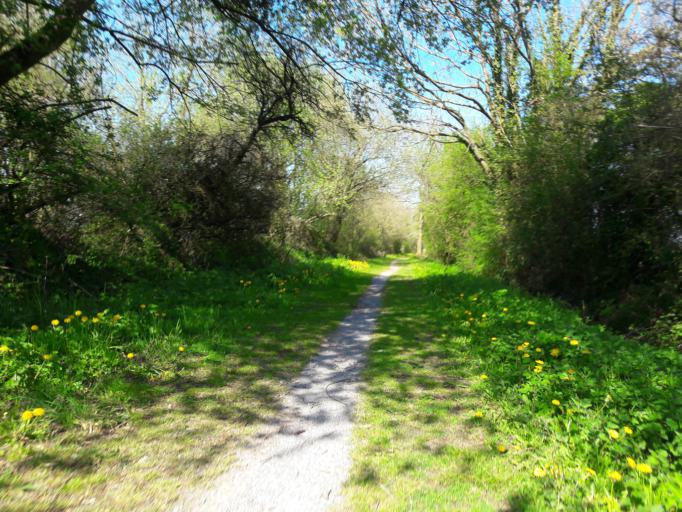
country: FR
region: Nord-Pas-de-Calais
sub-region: Departement du Nord
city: Sains-du-Nord
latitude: 50.1633
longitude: 4.0721
